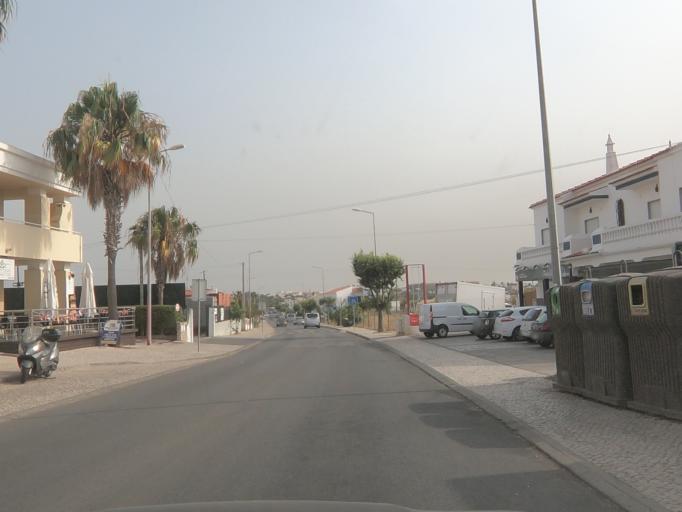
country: PT
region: Faro
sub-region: Albufeira
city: Guia
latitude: 37.0962
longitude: -8.3096
